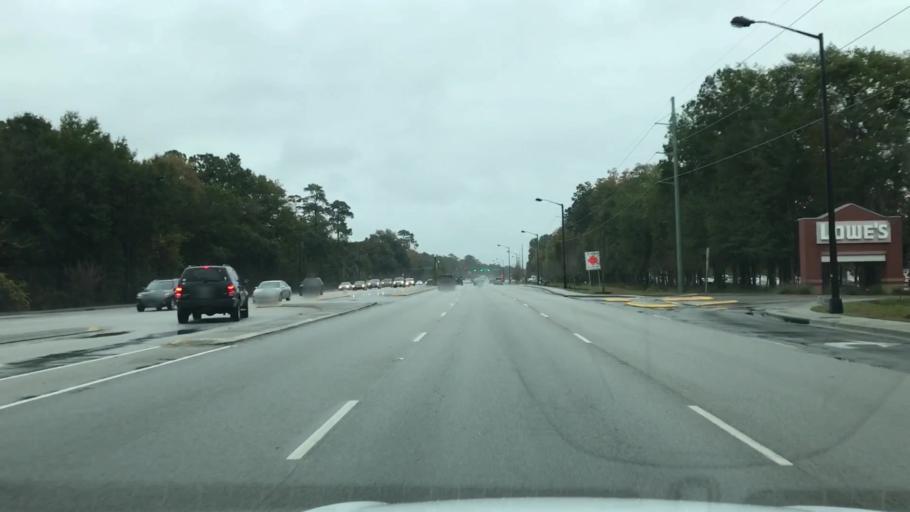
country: US
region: South Carolina
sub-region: Charleston County
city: Isle of Palms
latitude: 32.8701
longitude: -79.7789
